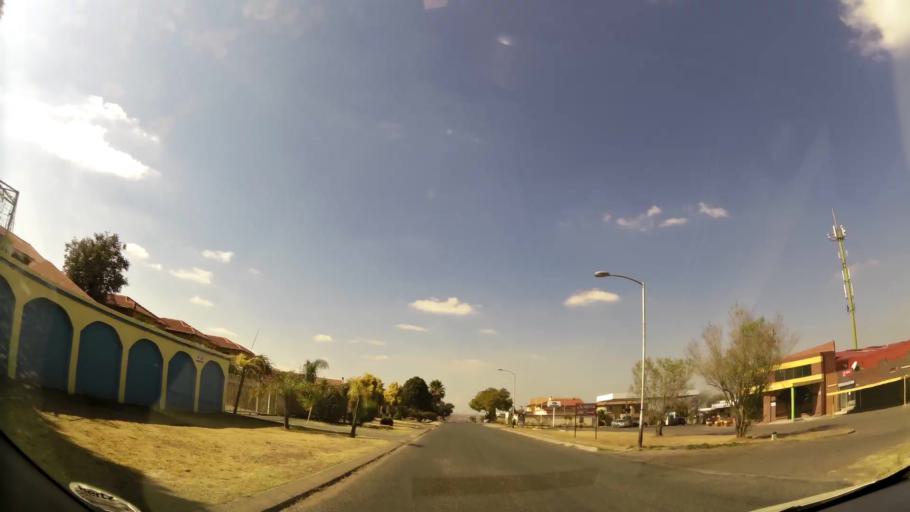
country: ZA
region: Gauteng
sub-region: West Rand District Municipality
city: Randfontein
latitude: -26.1698
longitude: 27.7482
